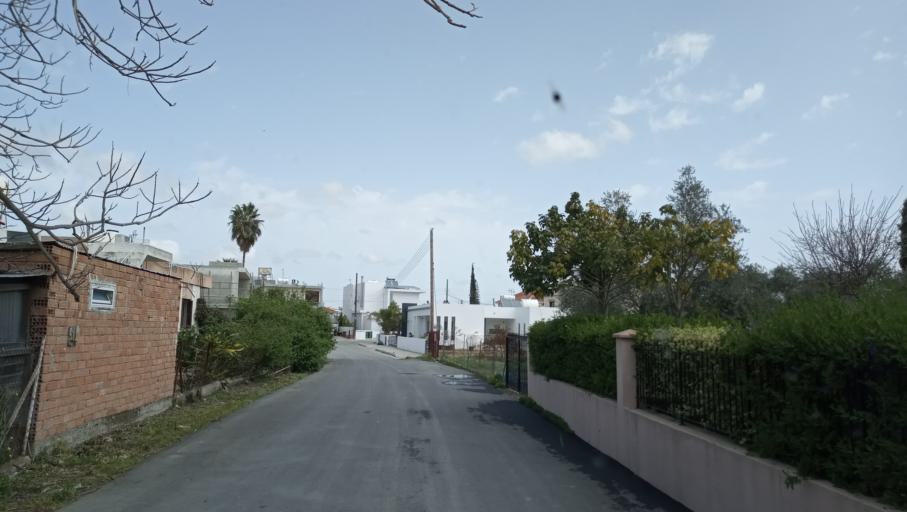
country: CY
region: Lefkosia
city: Dali
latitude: 35.0223
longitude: 33.4251
